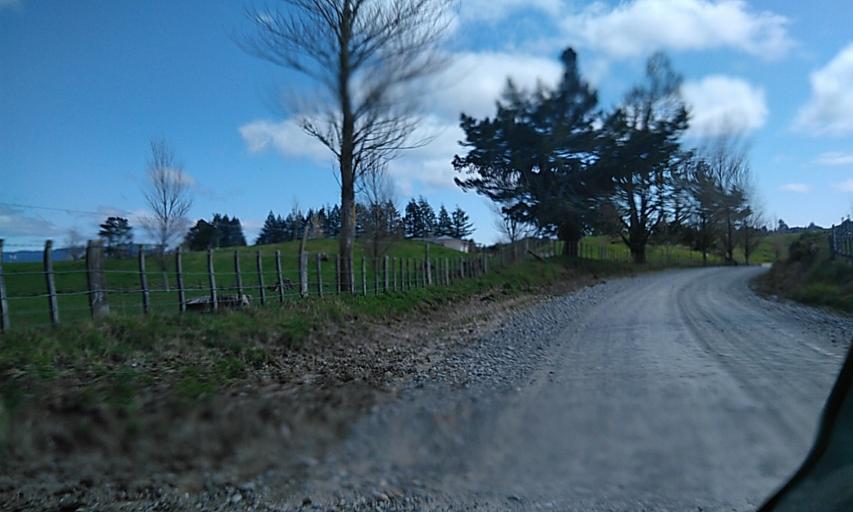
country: NZ
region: Gisborne
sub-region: Gisborne District
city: Gisborne
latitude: -38.2170
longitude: 178.0733
